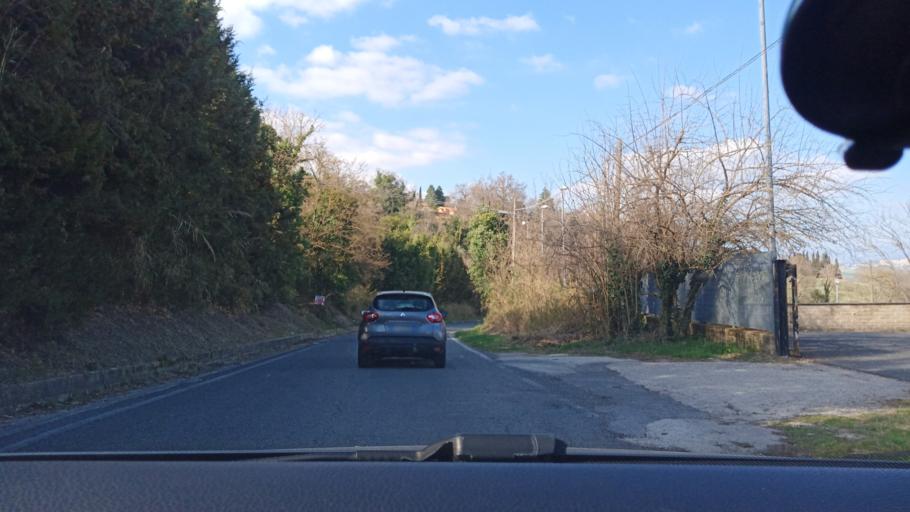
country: IT
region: Latium
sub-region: Citta metropolitana di Roma Capitale
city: Torrita Tiberina
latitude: 42.2403
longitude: 12.6169
